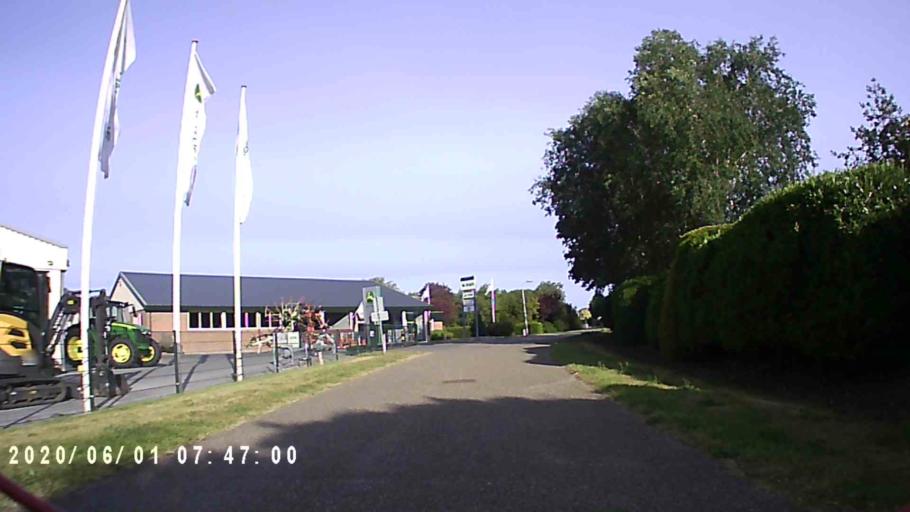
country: NL
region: Friesland
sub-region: Gemeente Dantumadiel
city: Rinsumageast
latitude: 53.2952
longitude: 5.9544
